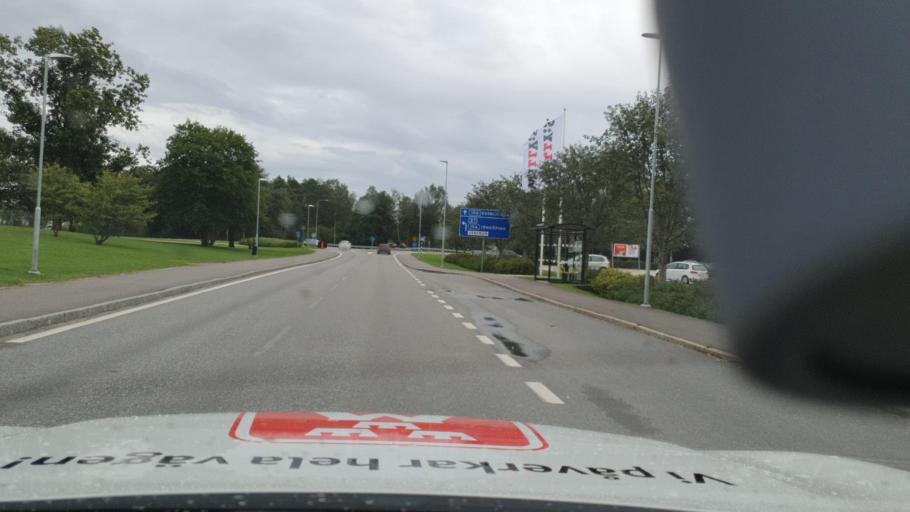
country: SE
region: Vaestra Goetaland
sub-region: Tranemo Kommun
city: Tranemo
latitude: 57.4888
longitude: 13.3409
